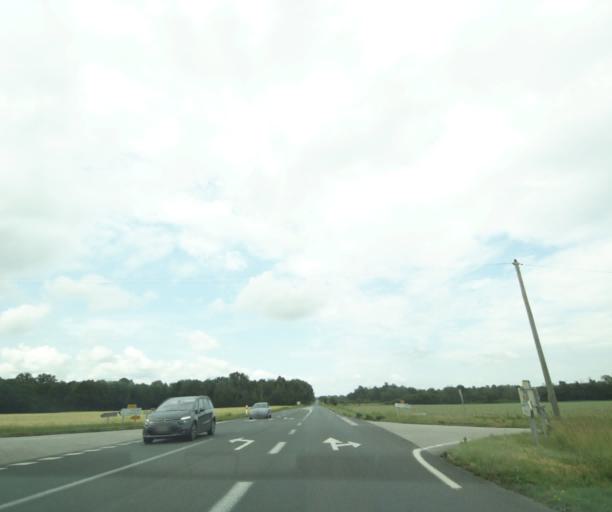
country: FR
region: Pays de la Loire
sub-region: Departement de Maine-et-Loire
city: Montreuil-Bellay
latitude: 47.0979
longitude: -0.1688
